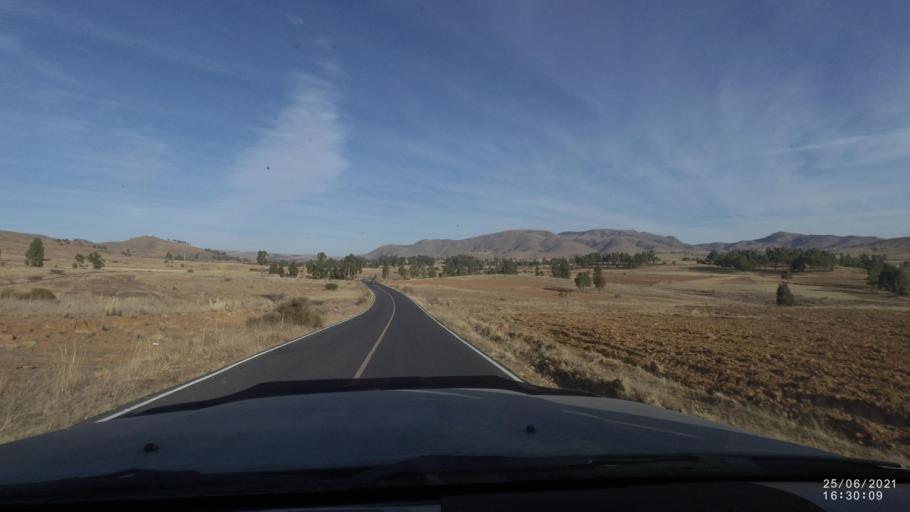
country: BO
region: Cochabamba
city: Arani
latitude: -17.7898
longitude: -65.8069
